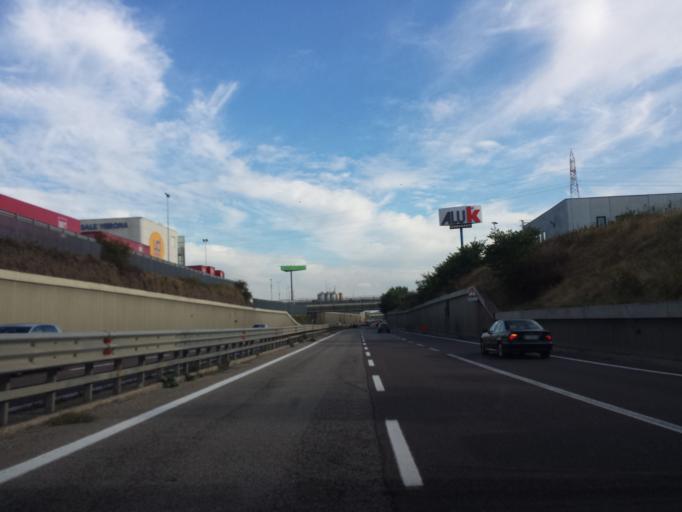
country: IT
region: Veneto
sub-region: Provincia di Verona
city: San Giovanni Lupatoto
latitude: 45.3978
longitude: 11.0142
